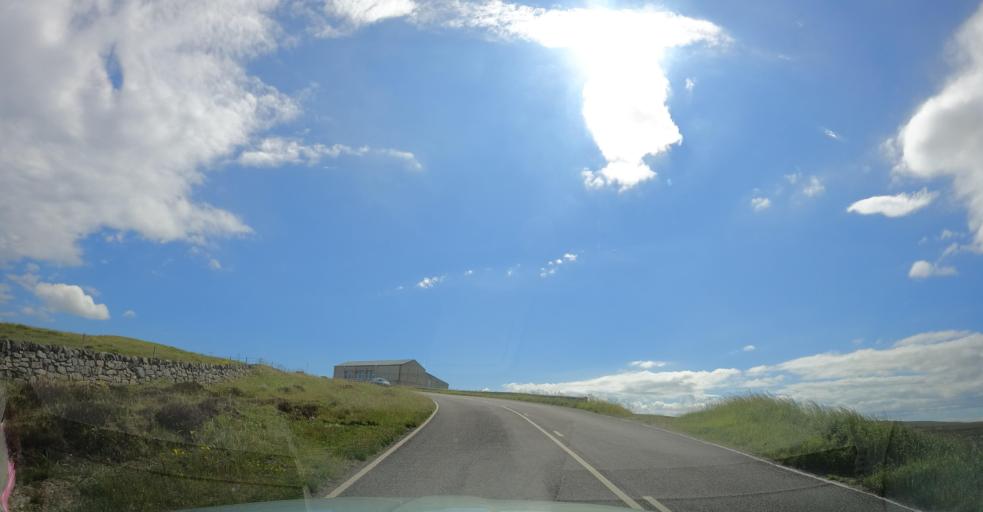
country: GB
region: Scotland
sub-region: Eilean Siar
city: Isle of Lewis
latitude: 58.4657
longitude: -6.3002
